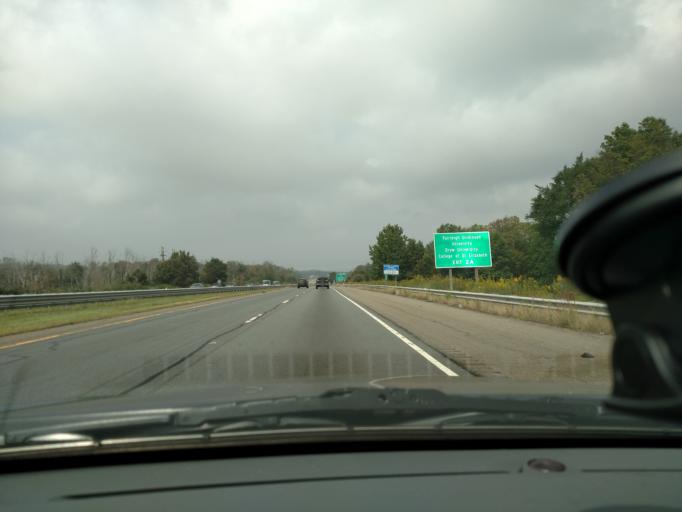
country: US
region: New Jersey
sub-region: Morris County
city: Madison
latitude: 40.7825
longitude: -74.4153
